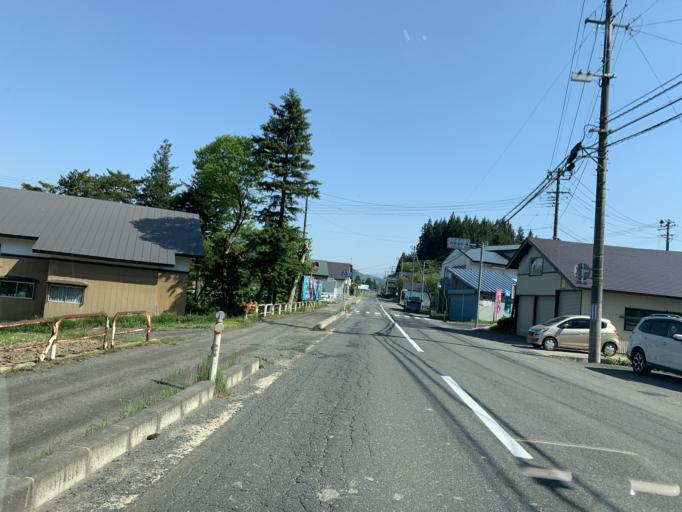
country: JP
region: Akita
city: Yokotemachi
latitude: 39.4077
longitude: 140.7516
